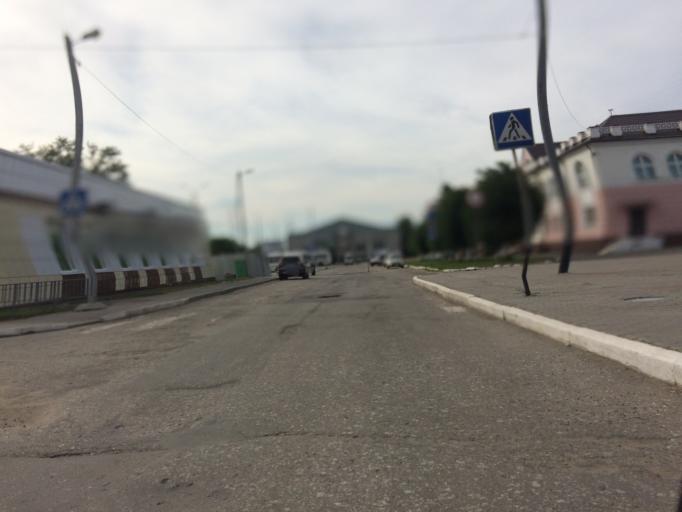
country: RU
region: Mariy-El
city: Yoshkar-Ola
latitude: 56.6219
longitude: 47.8808
